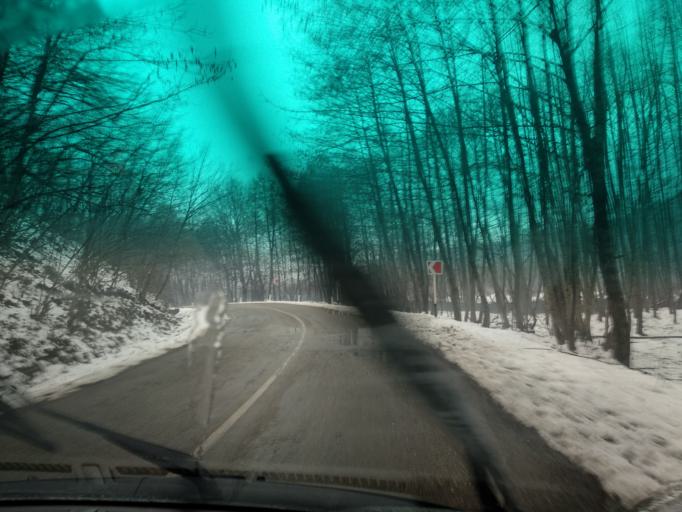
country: RU
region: Krasnodarskiy
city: Khadyzhensk
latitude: 44.2091
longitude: 39.4266
